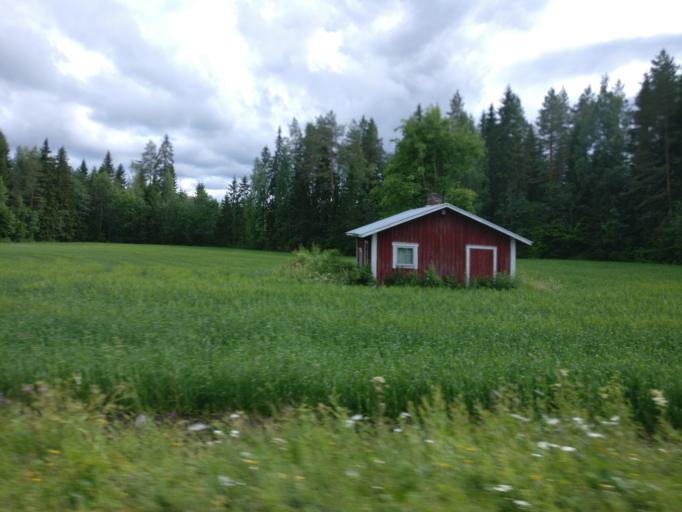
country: FI
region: Northern Savo
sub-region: Koillis-Savo
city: Juankoski
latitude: 62.9734
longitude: 28.2506
